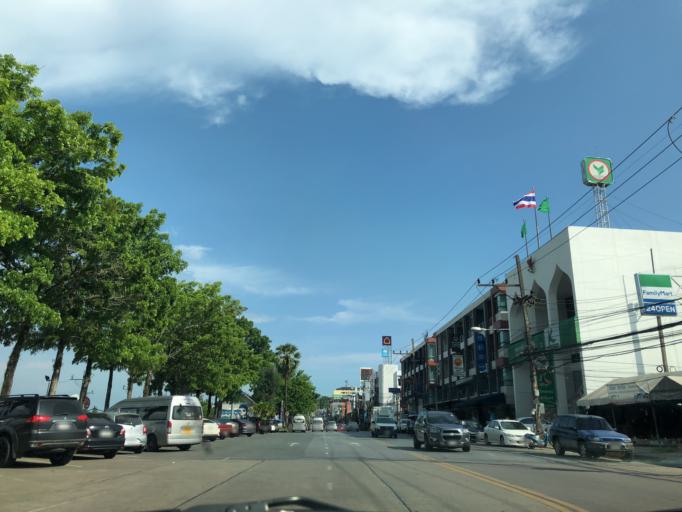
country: TH
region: Krabi
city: Krabi
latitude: 8.0664
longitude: 98.9171
